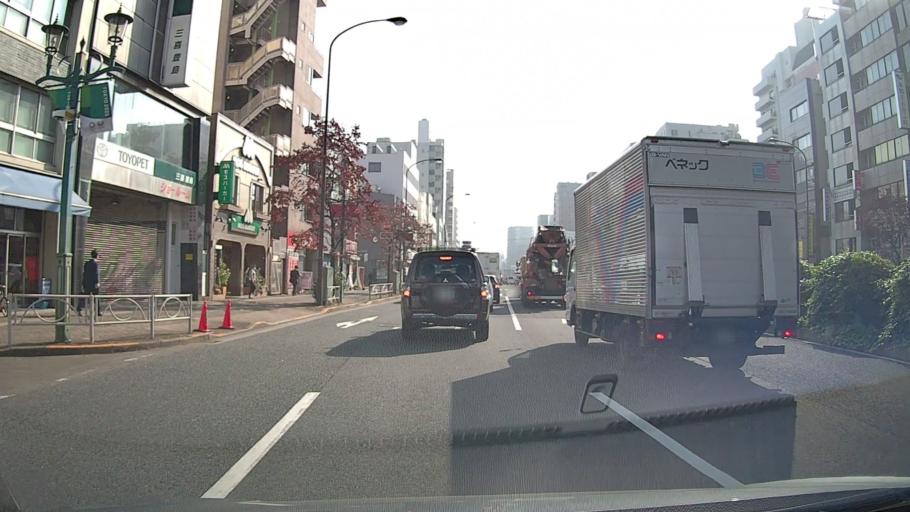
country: JP
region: Tokyo
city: Tokyo
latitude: 35.7317
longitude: 139.7408
